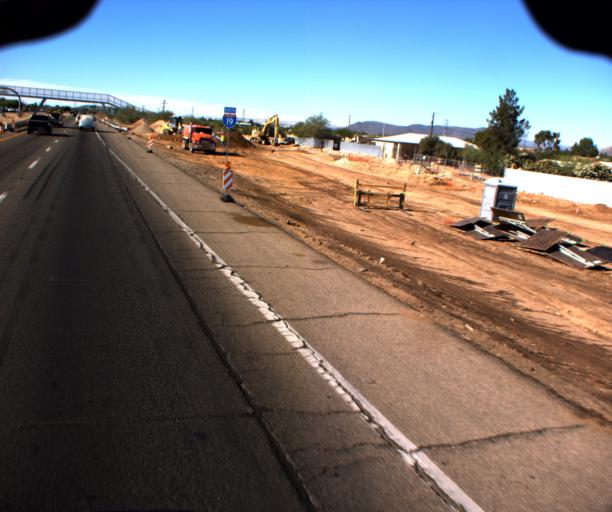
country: US
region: Arizona
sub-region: Pima County
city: South Tucson
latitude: 32.1727
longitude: -110.9858
